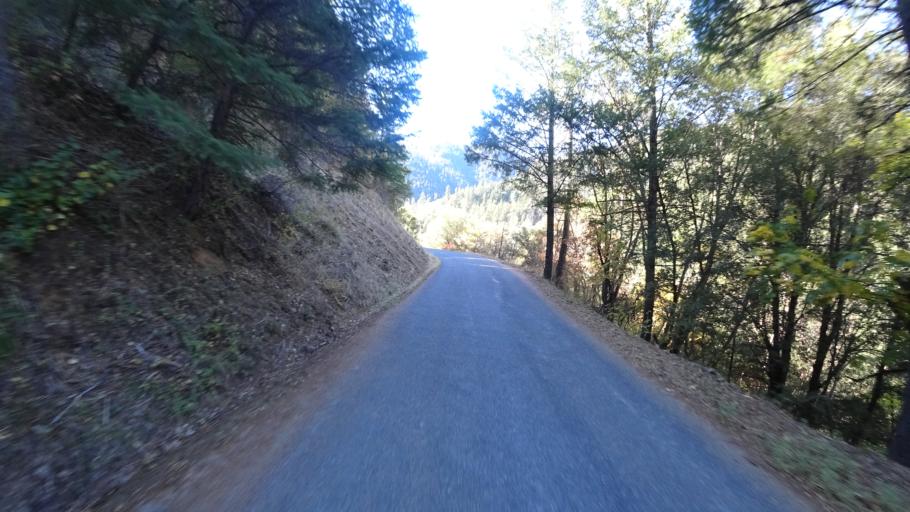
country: US
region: California
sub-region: Humboldt County
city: Willow Creek
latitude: 41.1729
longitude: -123.2194
